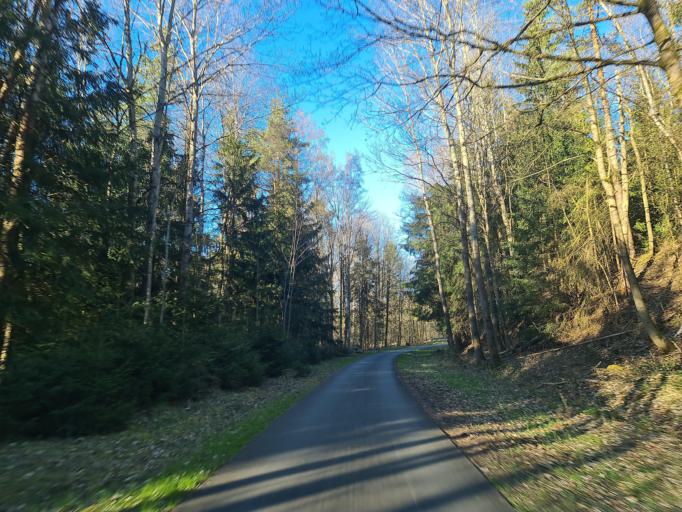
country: DE
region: Saxony
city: Neustadt Vogtland
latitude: 50.4752
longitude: 12.3114
